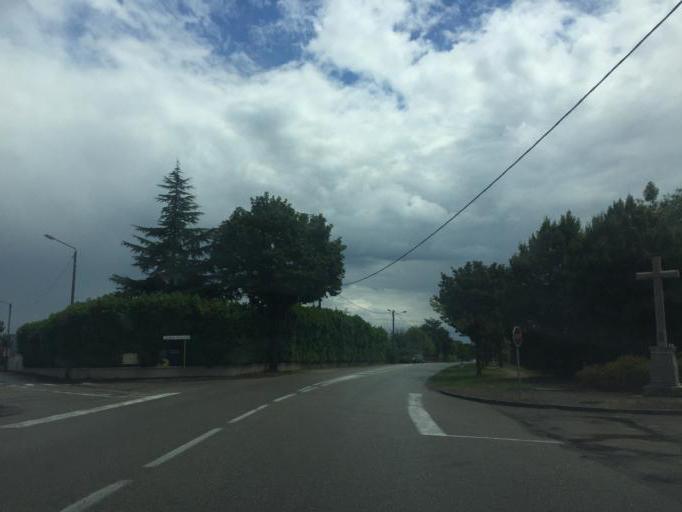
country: FR
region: Rhone-Alpes
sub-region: Departement de l'Isere
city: Janneyrias
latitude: 45.7941
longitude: 5.1258
